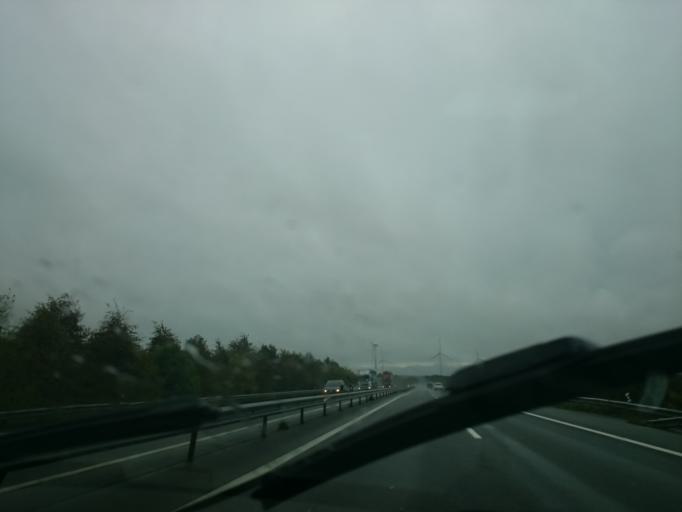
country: FR
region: Pays de la Loire
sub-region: Departement de la Loire-Atlantique
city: Besne
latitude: 47.4183
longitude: -2.0419
